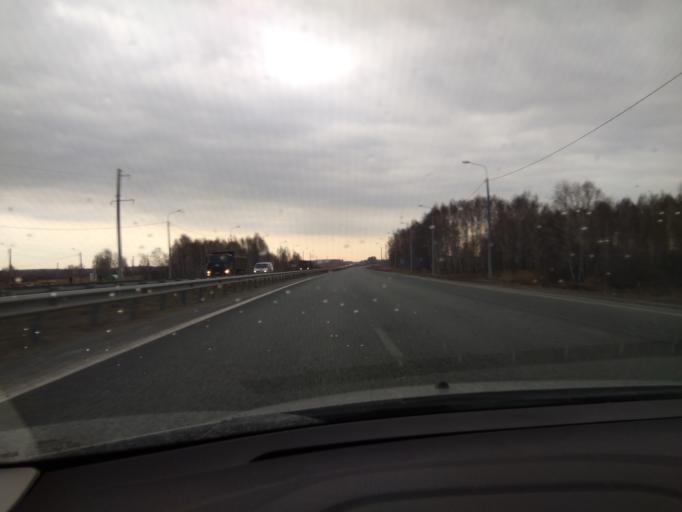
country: RU
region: Chelyabinsk
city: Kunashak
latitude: 55.7617
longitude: 61.2210
